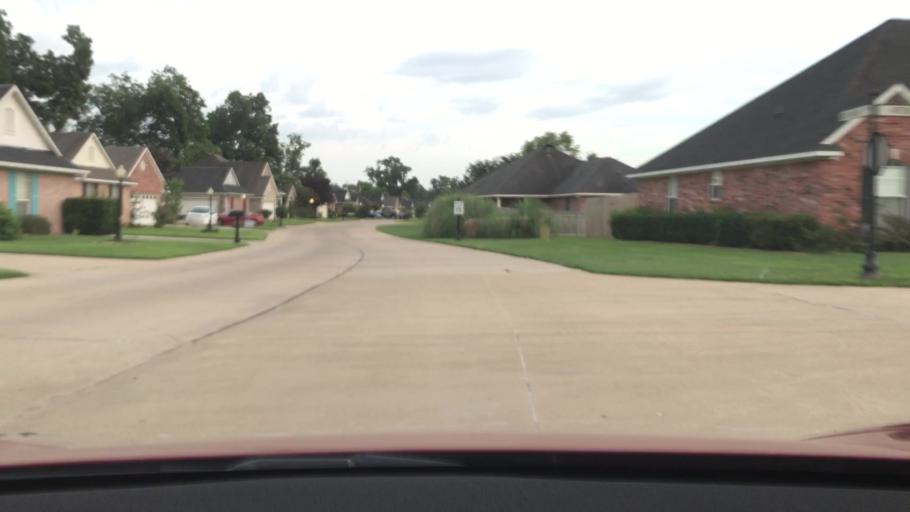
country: US
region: Louisiana
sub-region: Bossier Parish
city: Bossier City
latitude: 32.4531
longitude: -93.6671
